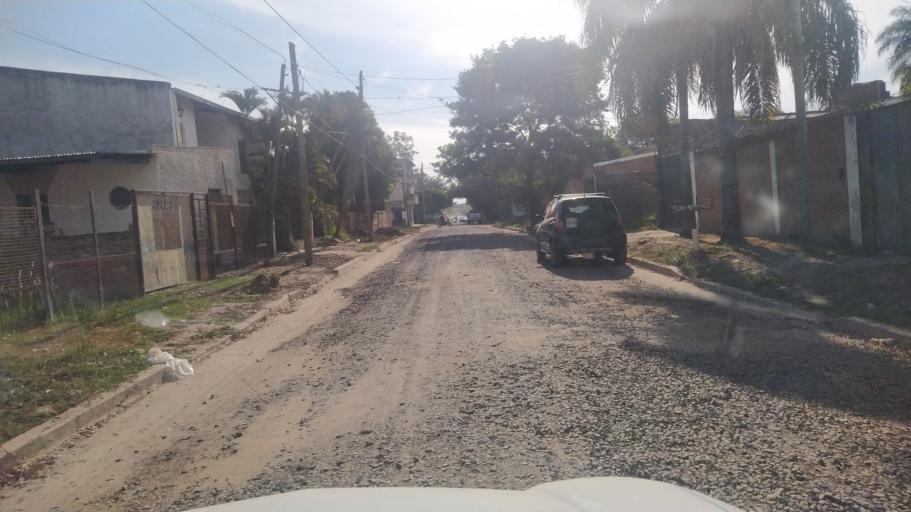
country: AR
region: Corrientes
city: Corrientes
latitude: -27.4878
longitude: -58.8141
